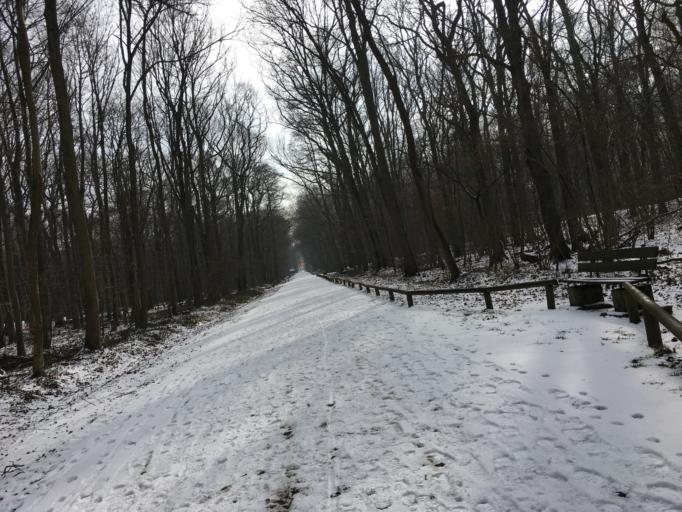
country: DE
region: North Rhine-Westphalia
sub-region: Regierungsbezirk Koln
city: Kreuzau
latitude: 50.7721
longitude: 6.5009
